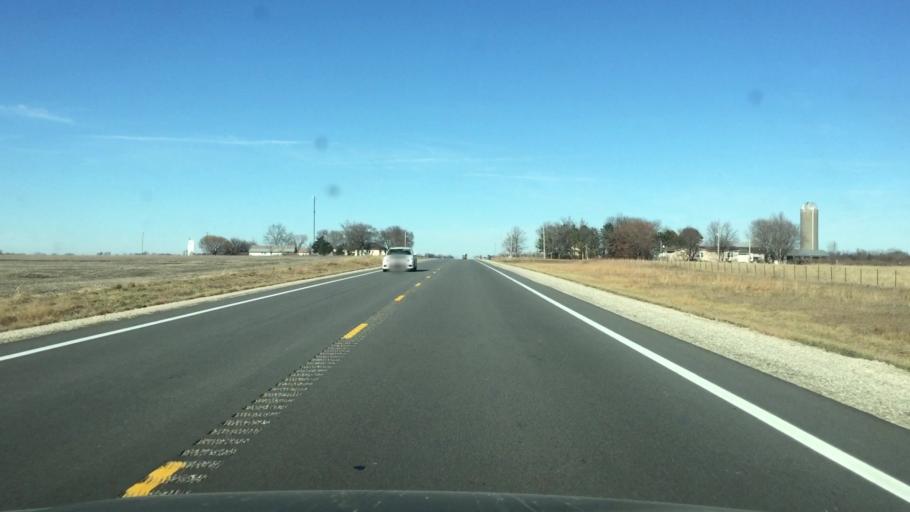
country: US
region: Kansas
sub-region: Anderson County
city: Garnett
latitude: 38.3811
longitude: -95.2488
